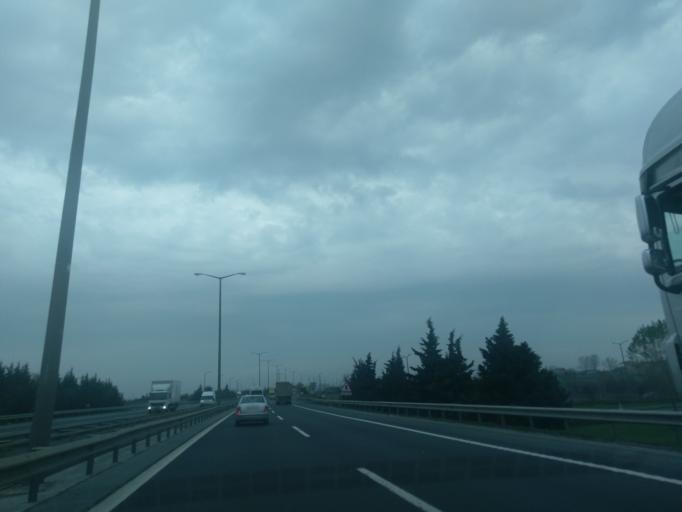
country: TR
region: Istanbul
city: Muratbey
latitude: 41.0872
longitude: 28.5083
